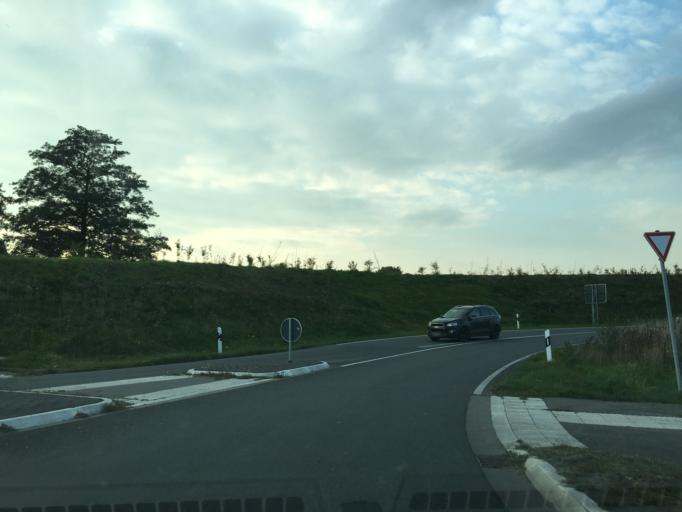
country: DE
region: North Rhine-Westphalia
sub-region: Regierungsbezirk Munster
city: Altenberge
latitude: 52.0429
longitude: 7.4845
